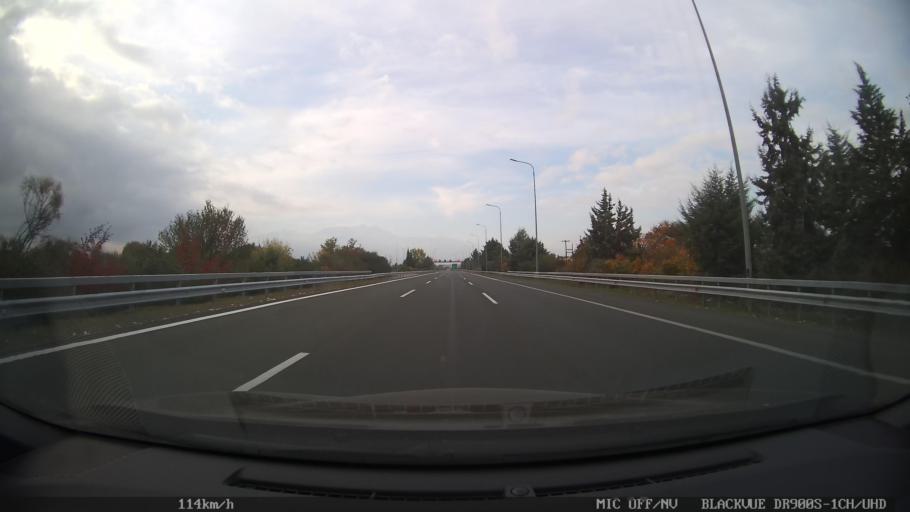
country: GR
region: Central Macedonia
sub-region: Nomos Pierias
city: Peristasi
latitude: 40.2838
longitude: 22.5266
